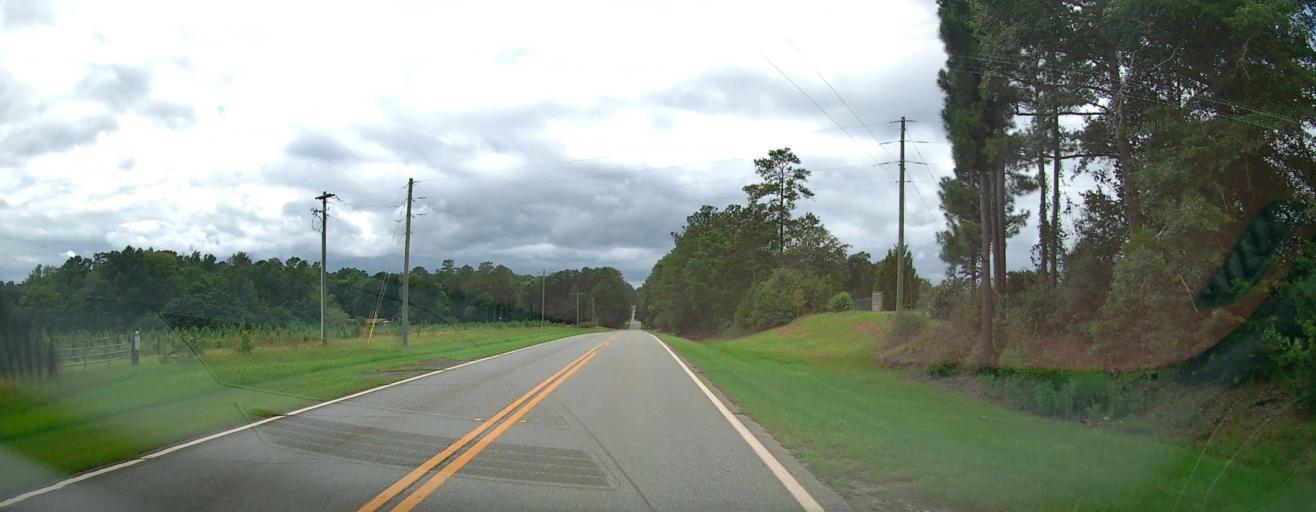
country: US
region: Georgia
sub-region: Twiggs County
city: Jeffersonville
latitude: 32.6799
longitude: -83.3161
